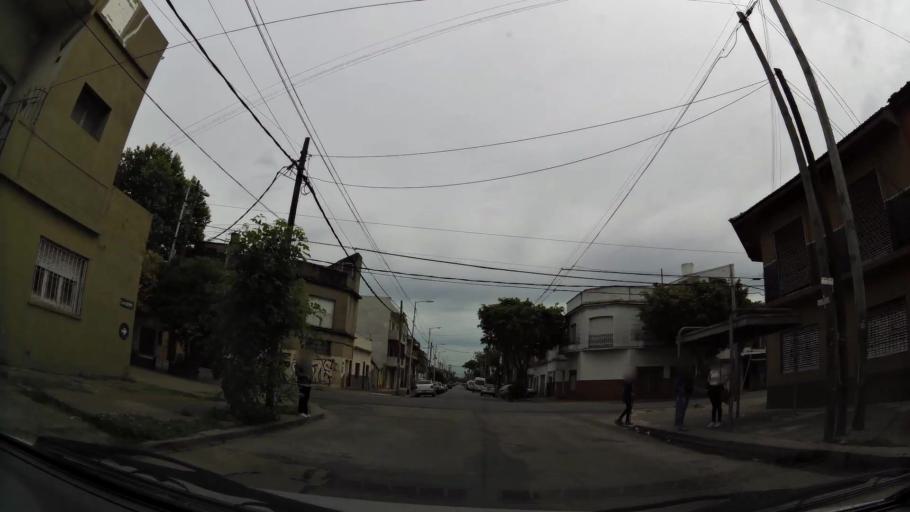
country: AR
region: Buenos Aires
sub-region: Partido de Avellaneda
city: Avellaneda
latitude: -34.6658
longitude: -58.3474
